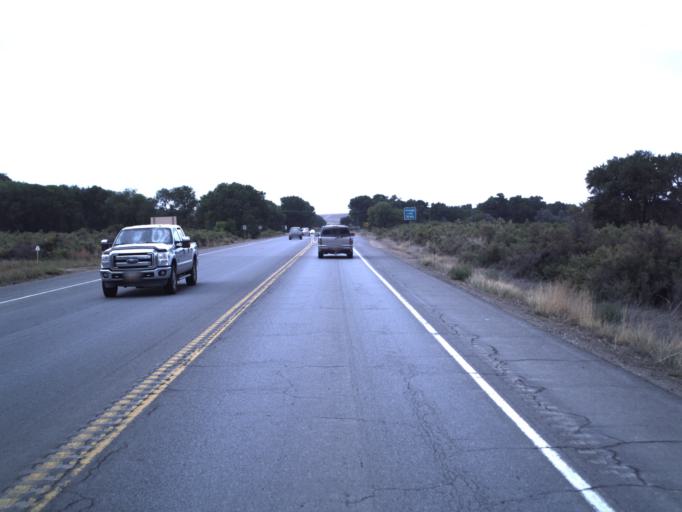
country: US
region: Utah
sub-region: Duchesne County
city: Duchesne
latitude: 40.1544
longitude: -110.2136
